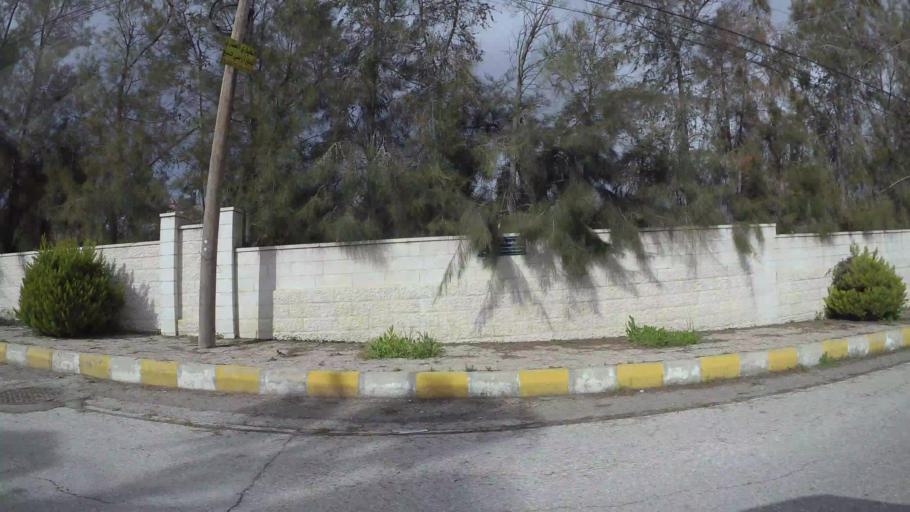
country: JO
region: Amman
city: Wadi as Sir
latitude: 31.9916
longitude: 35.8239
